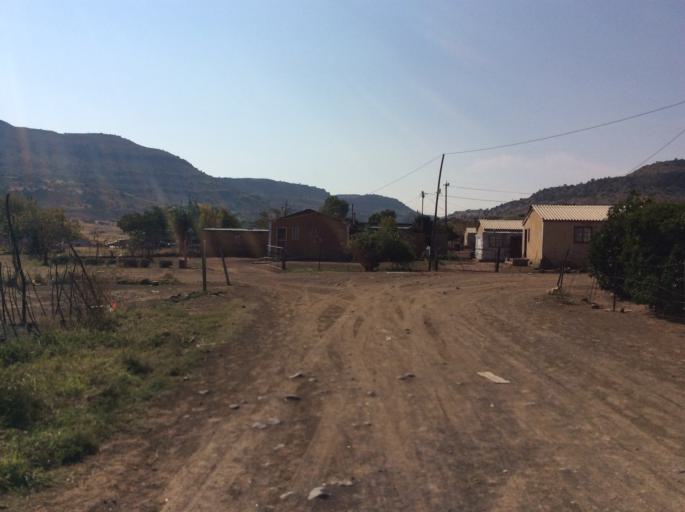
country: LS
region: Mafeteng
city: Mafeteng
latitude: -29.7162
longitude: 27.0287
